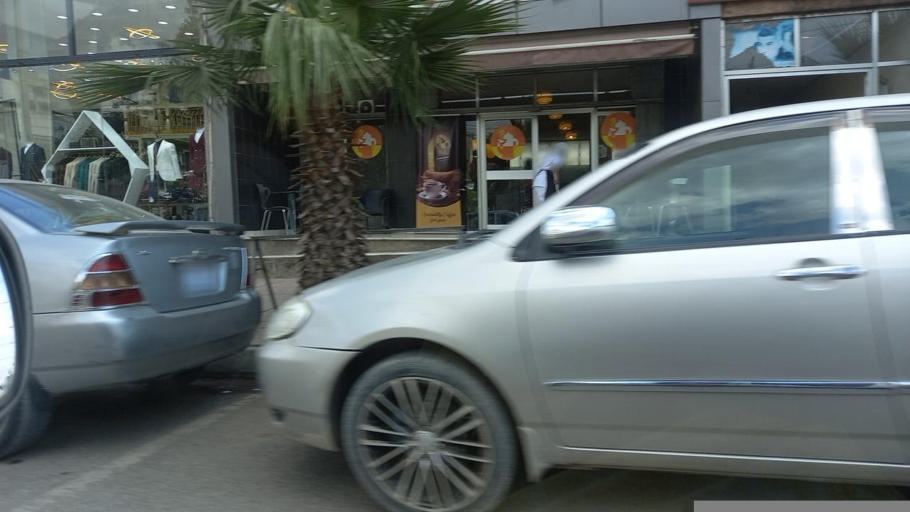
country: ET
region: Adis Abeba
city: Addis Ababa
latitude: 8.9945
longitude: 38.7286
